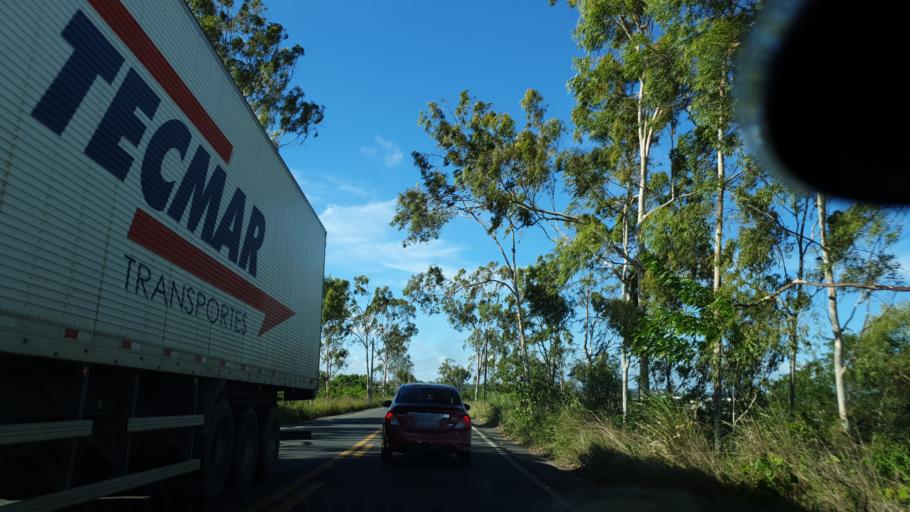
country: BR
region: Bahia
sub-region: Camacari
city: Camacari
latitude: -12.6550
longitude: -38.3028
